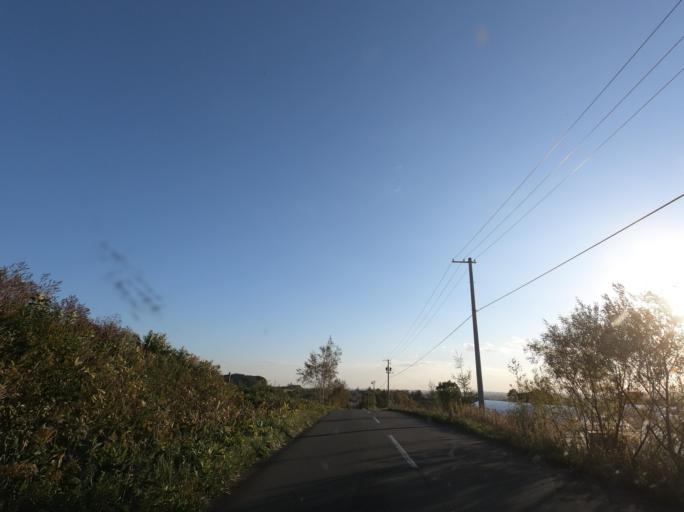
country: JP
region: Hokkaido
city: Iwamizawa
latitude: 43.0092
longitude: 141.8809
